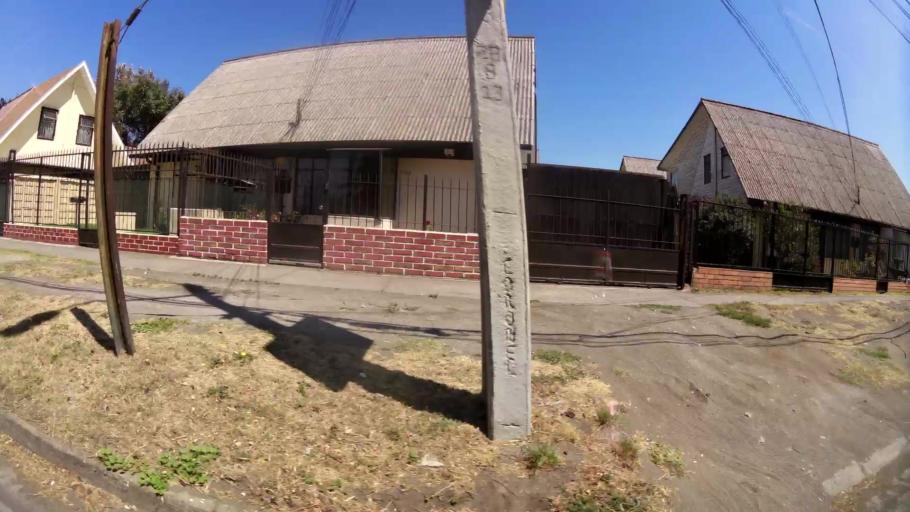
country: CL
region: Biobio
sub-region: Provincia de Concepcion
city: Concepcion
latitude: -36.8065
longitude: -73.0700
